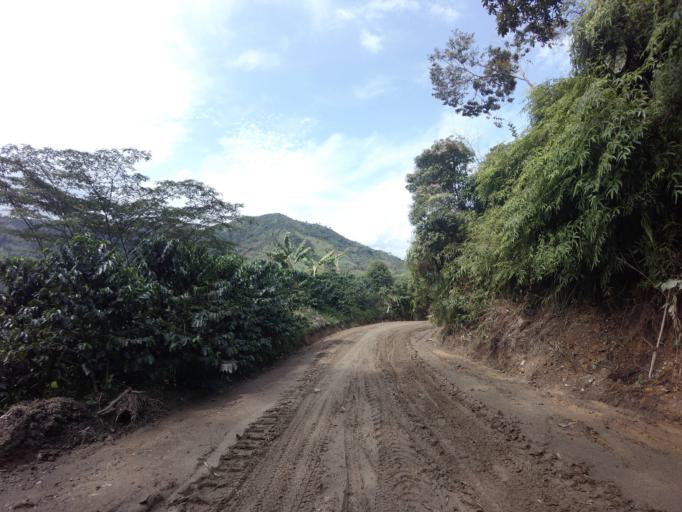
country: CO
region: Caldas
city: Marquetalia
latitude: 5.3303
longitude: -75.0450
